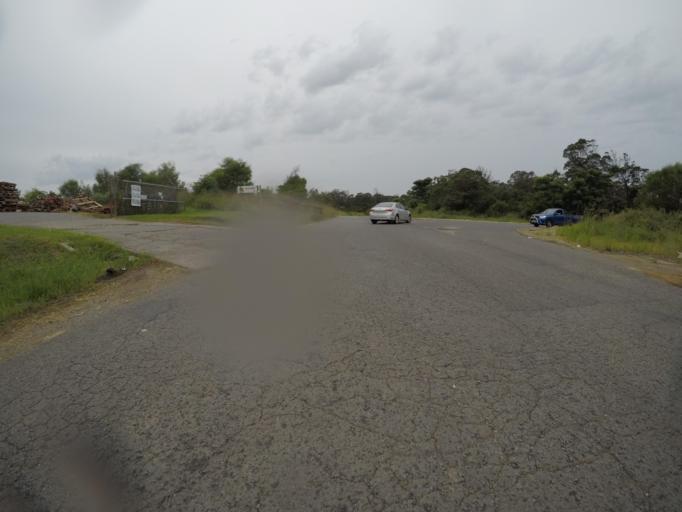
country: ZA
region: Eastern Cape
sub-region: Buffalo City Metropolitan Municipality
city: East London
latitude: -32.9864
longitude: 27.8269
